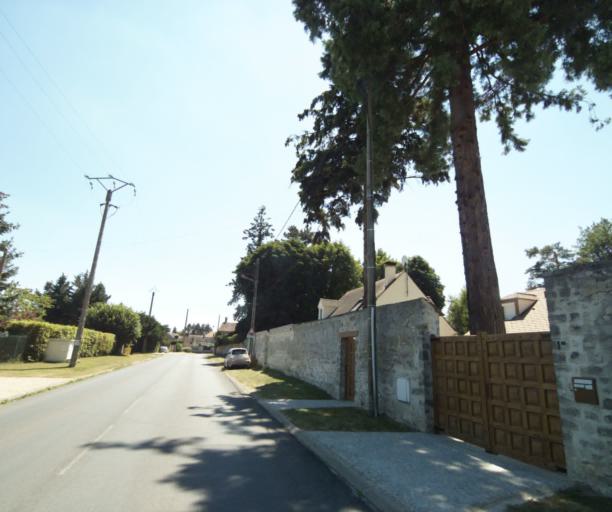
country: FR
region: Ile-de-France
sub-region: Departement de Seine-et-Marne
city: Noisy-sur-Ecole
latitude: 48.3606
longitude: 2.5200
